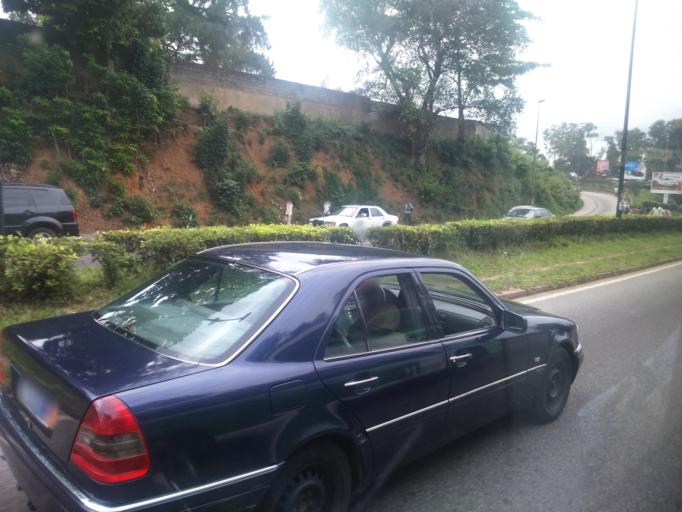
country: CI
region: Lagunes
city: Abidjan
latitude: 5.3556
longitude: -4.0016
